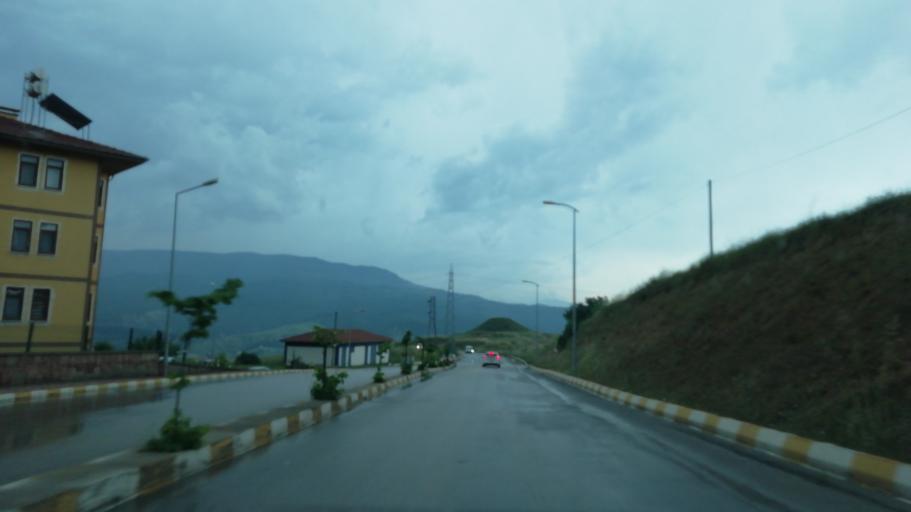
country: TR
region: Karabuk
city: Safranbolu
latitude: 41.2376
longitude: 32.6827
